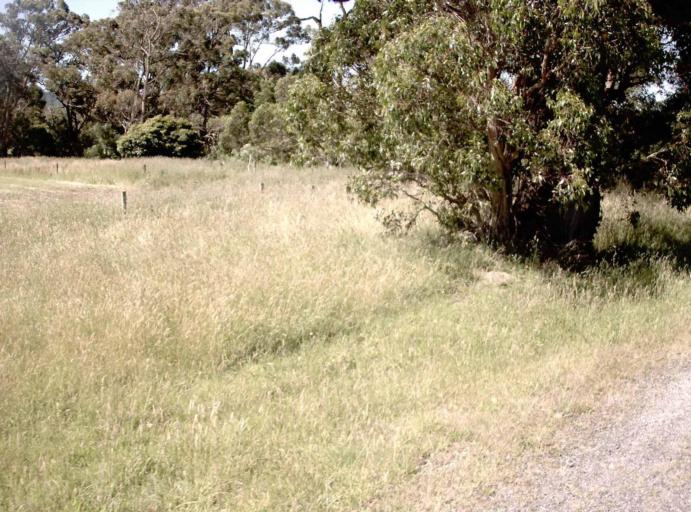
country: AU
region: Victoria
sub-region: Latrobe
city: Morwell
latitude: -38.6443
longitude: 146.4804
